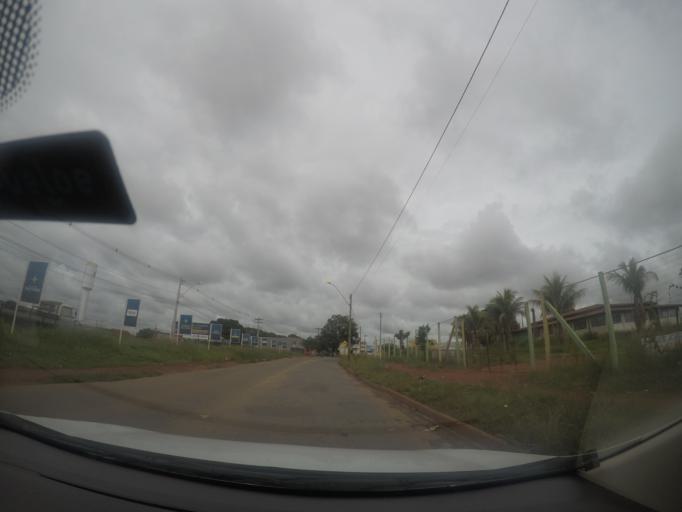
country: BR
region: Goias
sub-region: Goiania
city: Goiania
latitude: -16.6854
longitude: -49.3695
